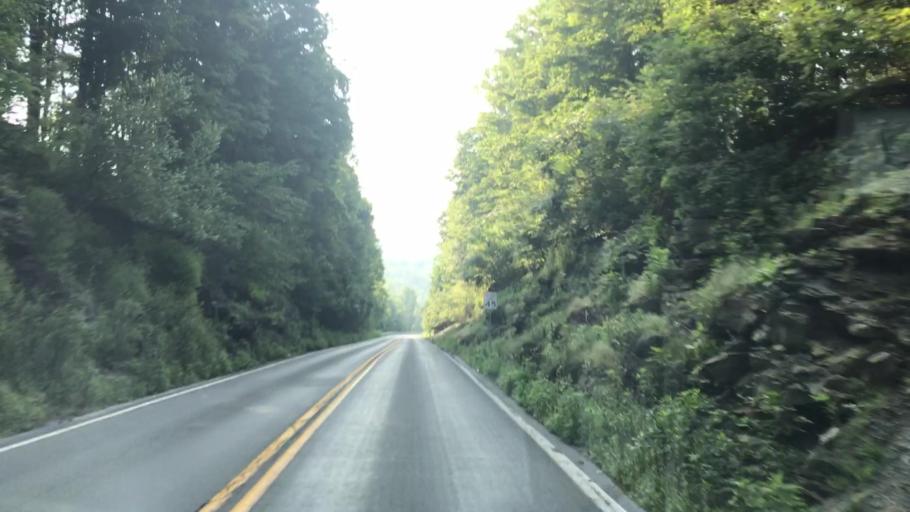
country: US
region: Pennsylvania
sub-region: Lackawanna County
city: Dalton
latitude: 41.5986
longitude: -75.6775
